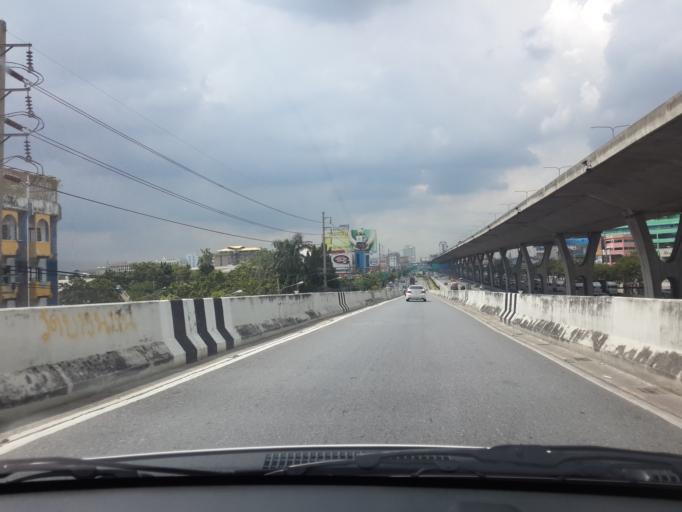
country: TH
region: Bangkok
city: Bang Na
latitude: 13.6702
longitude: 100.6204
